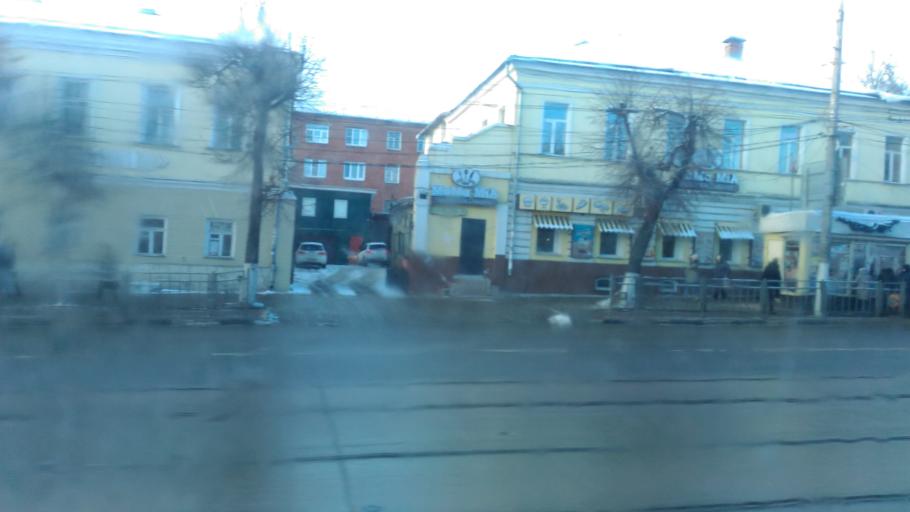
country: RU
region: Tula
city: Tula
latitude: 54.2063
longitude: 37.6193
